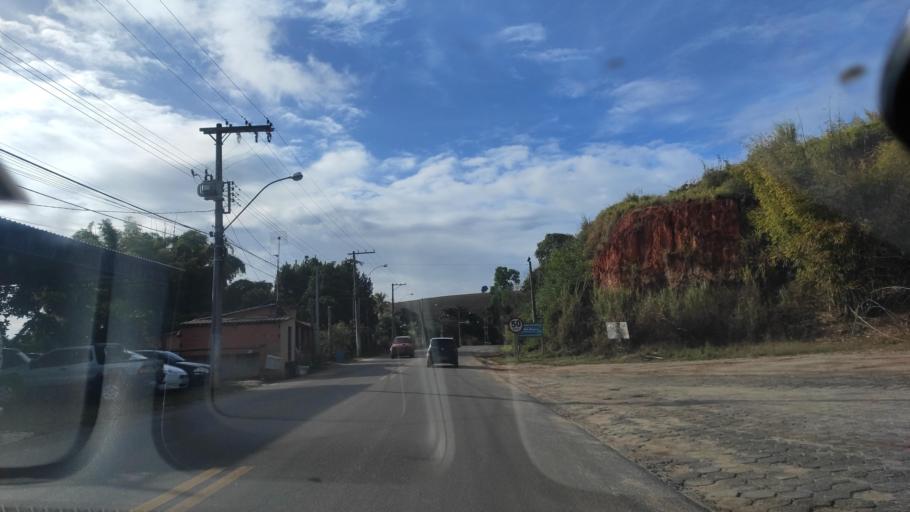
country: BR
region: Espirito Santo
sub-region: Nova Venecia
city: Nova Venecia
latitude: -18.7130
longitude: -40.3801
